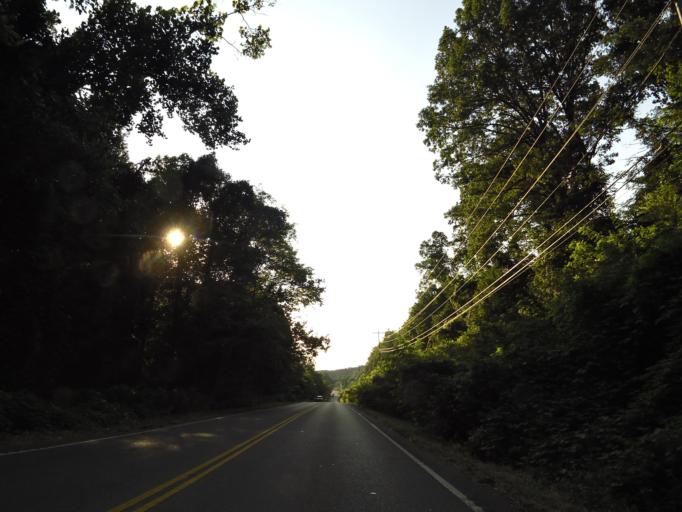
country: US
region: Tennessee
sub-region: McMinn County
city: Athens
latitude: 35.4264
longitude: -84.5679
